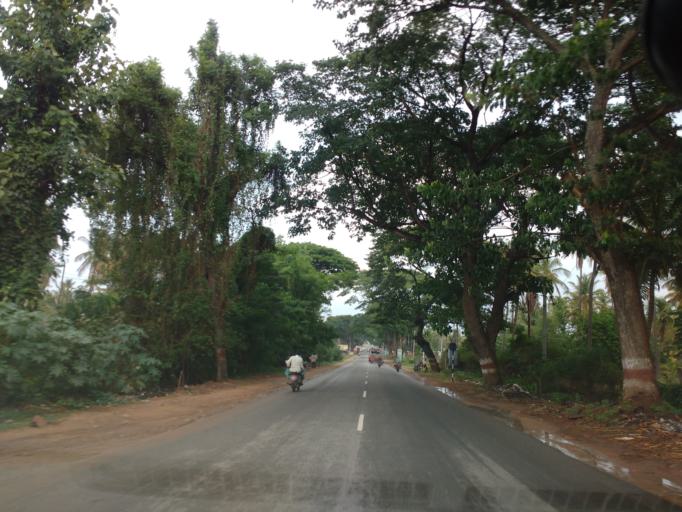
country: IN
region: Karnataka
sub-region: Hassan
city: Arsikere
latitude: 13.3330
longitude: 76.2419
